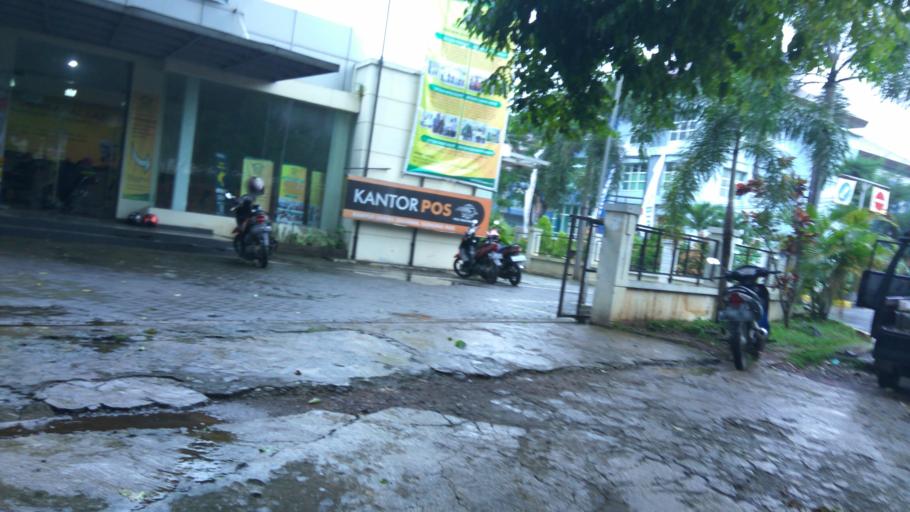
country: ID
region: Central Java
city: Semarang
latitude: -7.0488
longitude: 110.3952
